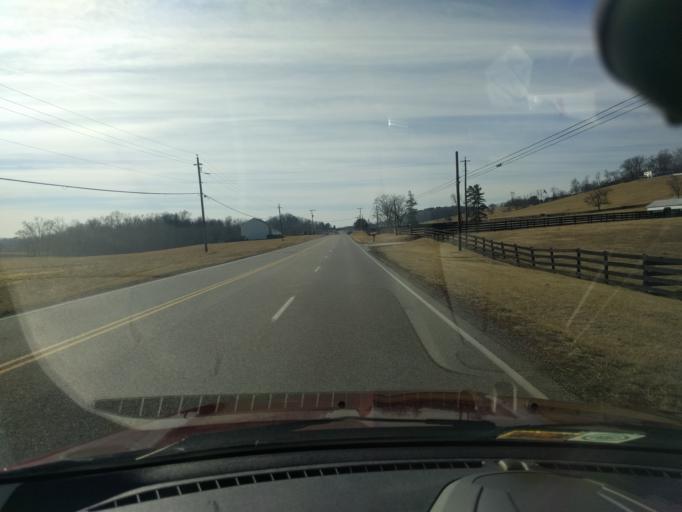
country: US
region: Virginia
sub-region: Augusta County
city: Weyers Cave
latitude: 38.2771
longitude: -78.9441
